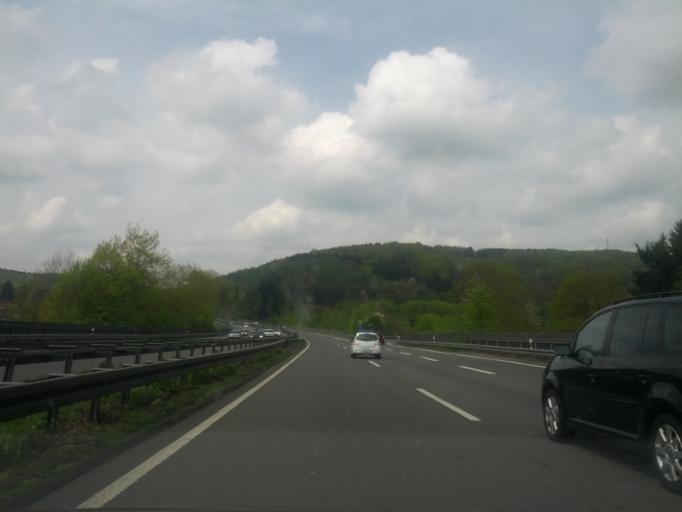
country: DE
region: North Rhine-Westphalia
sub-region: Regierungsbezirk Koln
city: Overath
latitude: 50.9469
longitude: 7.2217
